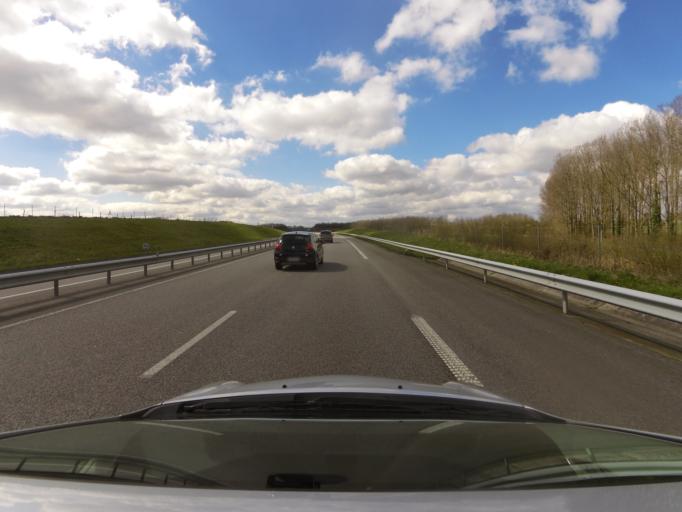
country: FR
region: Haute-Normandie
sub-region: Departement de la Seine-Maritime
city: Yerville
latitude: 49.6628
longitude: 0.9208
